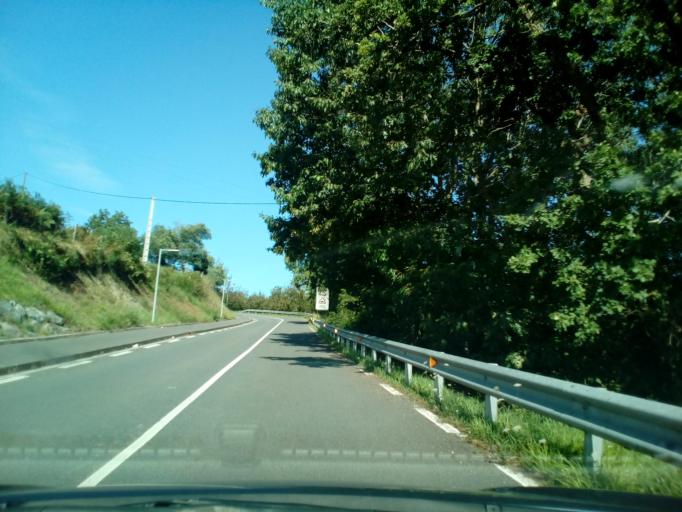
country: ES
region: Basque Country
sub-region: Provincia de Guipuzcoa
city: Aduna
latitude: 43.2014
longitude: -2.0496
